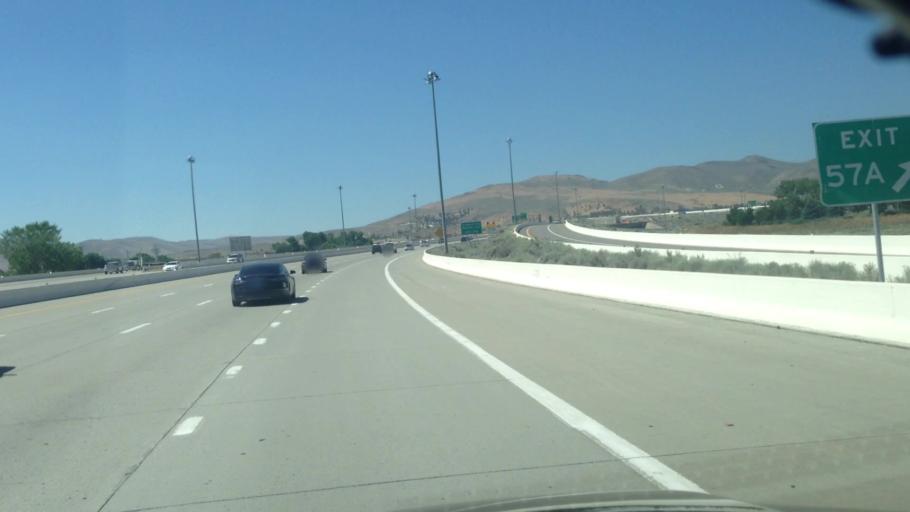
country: US
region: Nevada
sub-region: Washoe County
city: Sparks
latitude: 39.4140
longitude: -119.7473
